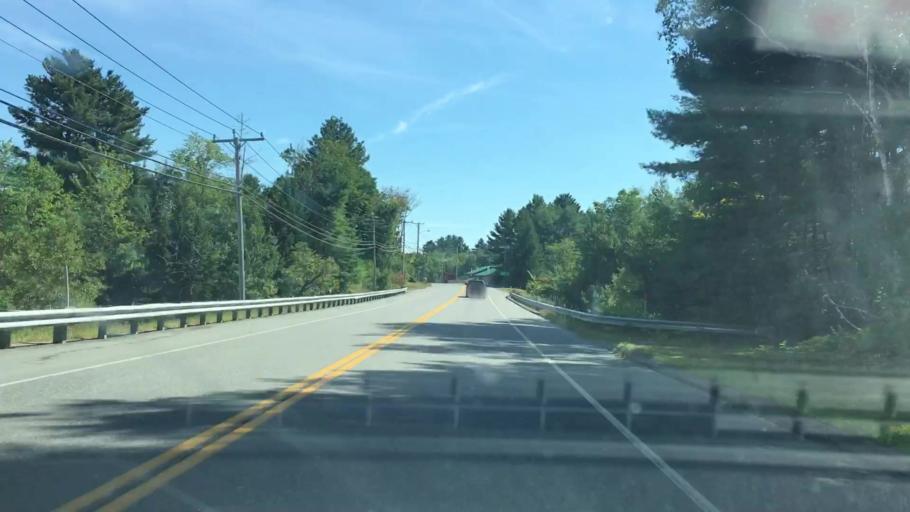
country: US
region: Maine
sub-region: Piscataquis County
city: Milo
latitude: 45.2440
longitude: -68.9745
